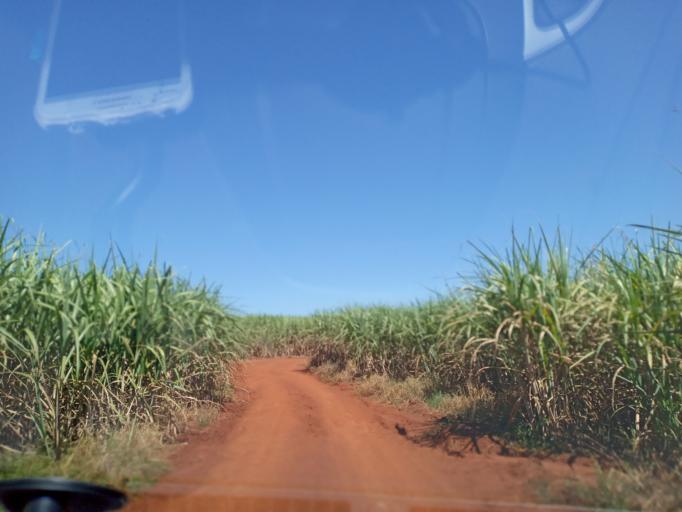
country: BR
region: Goias
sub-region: Itumbiara
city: Itumbiara
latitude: -18.4368
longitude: -49.1485
